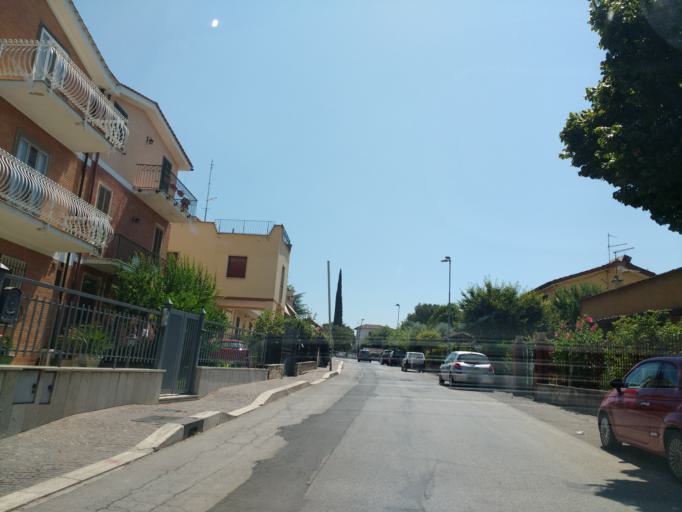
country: IT
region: Latium
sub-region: Citta metropolitana di Roma Capitale
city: Villa Adriana
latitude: 41.9488
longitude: 12.7729
